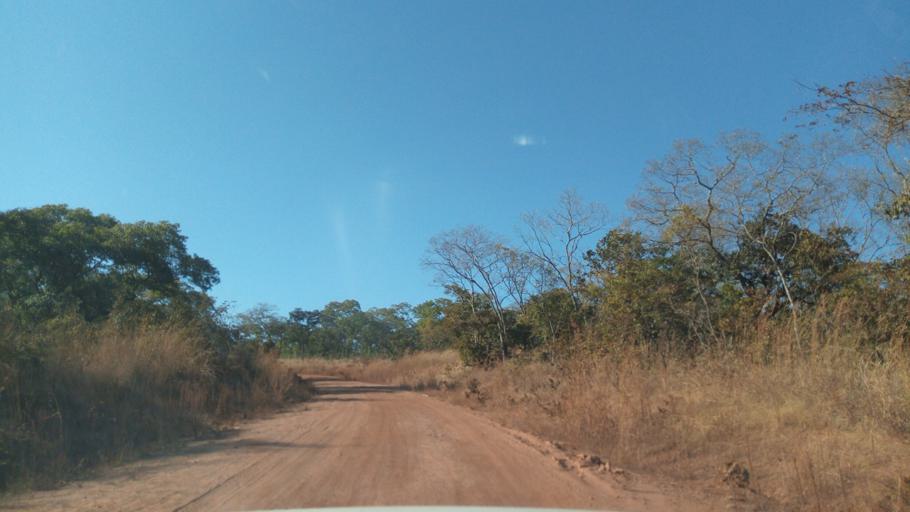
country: ZM
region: Luapula
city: Mwense
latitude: -10.5806
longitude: 28.4335
